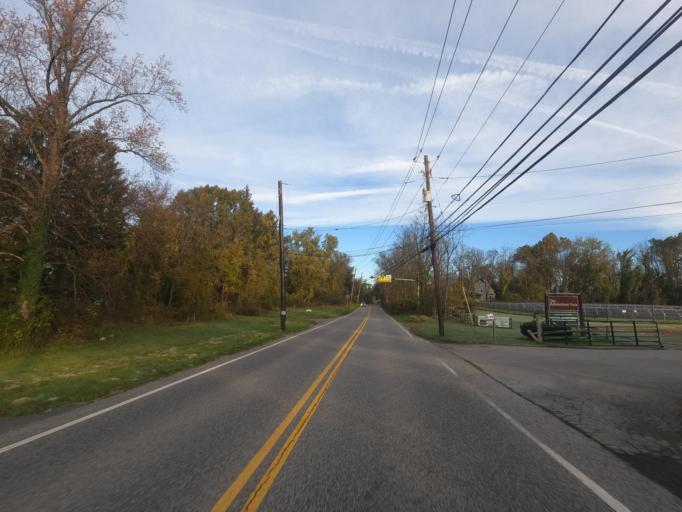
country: US
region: Maryland
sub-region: Montgomery County
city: Ashton-Sandy Spring
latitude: 39.1301
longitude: -77.0293
